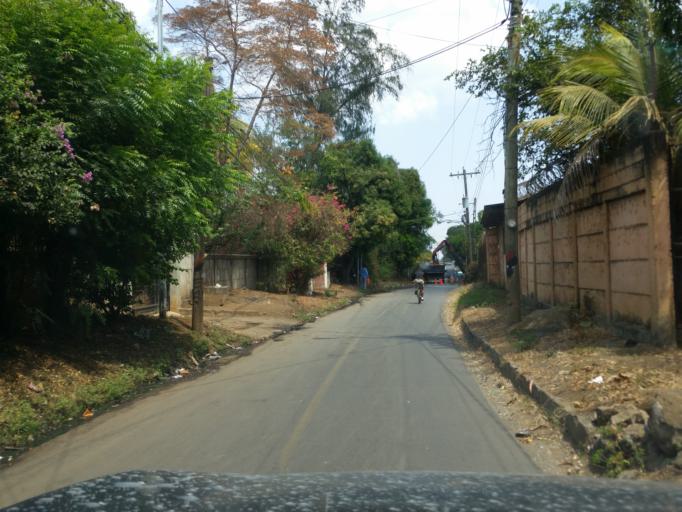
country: NI
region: Masaya
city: Ticuantepe
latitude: 12.0654
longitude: -86.2079
